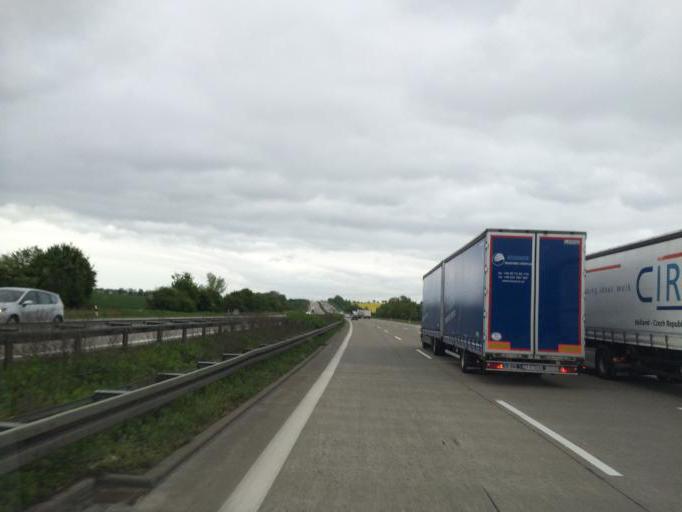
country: DE
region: Saxony-Anhalt
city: Wefensleben
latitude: 52.2026
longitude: 11.1896
